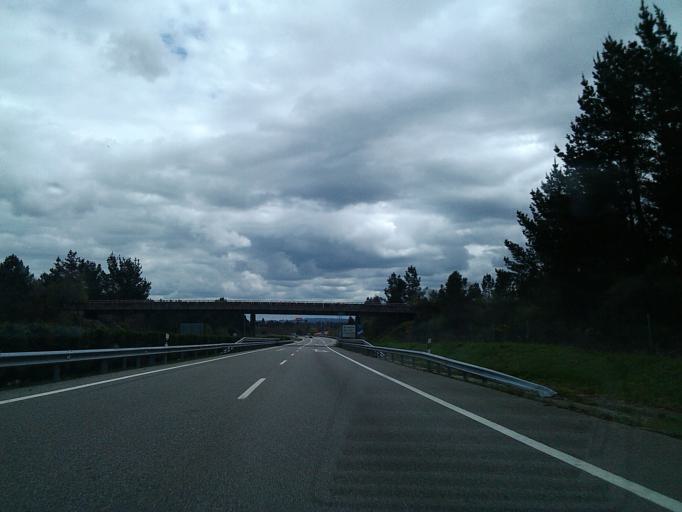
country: ES
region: Galicia
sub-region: Provincia de Lugo
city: Guitiriz
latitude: 43.1900
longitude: -7.9358
